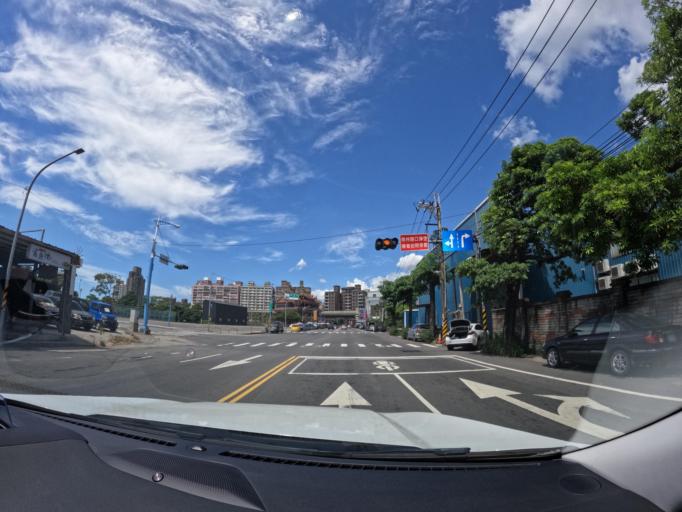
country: TW
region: Taipei
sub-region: Taipei
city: Banqiao
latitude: 25.1422
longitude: 121.3957
